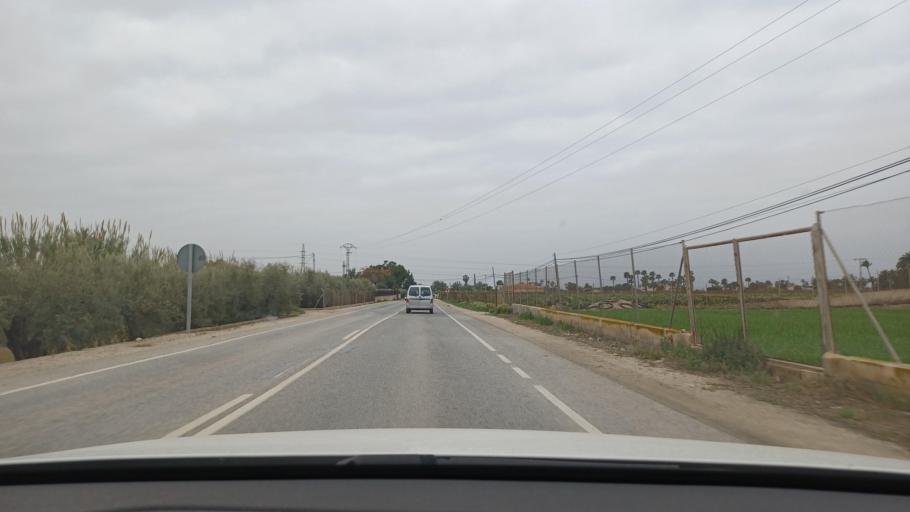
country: ES
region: Valencia
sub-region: Provincia de Alicante
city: Elche
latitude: 38.2365
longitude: -0.7141
